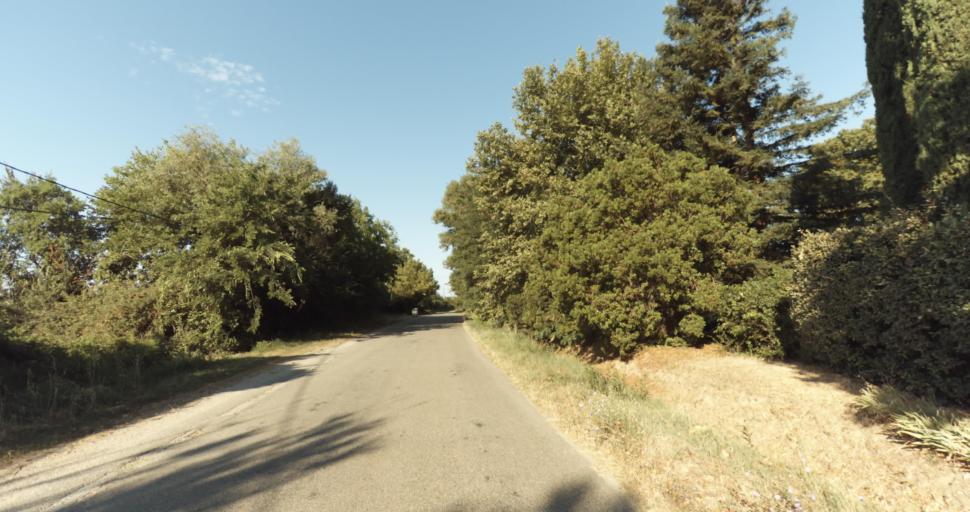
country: FR
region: Provence-Alpes-Cote d'Azur
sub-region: Departement du Vaucluse
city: Sarrians
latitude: 44.0534
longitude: 4.9633
